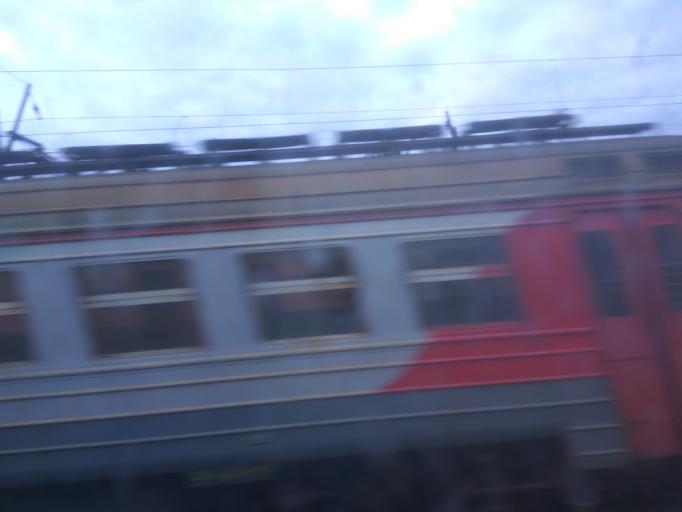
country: RU
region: Moskovskaya
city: Aprelevka
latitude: 55.5576
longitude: 37.0848
